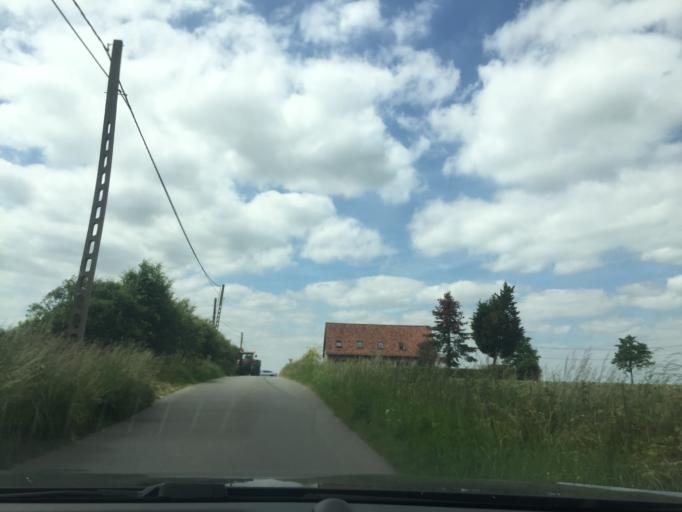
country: BE
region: Flanders
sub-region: Provincie West-Vlaanderen
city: Zwevegem
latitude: 50.7880
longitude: 3.3190
